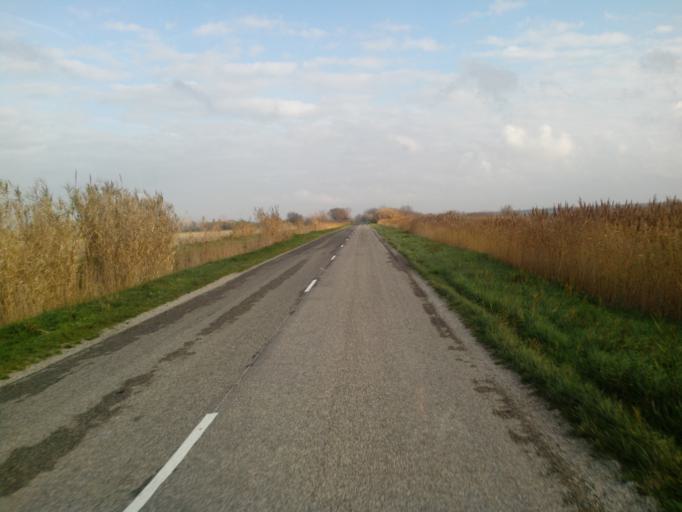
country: FR
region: Provence-Alpes-Cote d'Azur
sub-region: Departement des Bouches-du-Rhone
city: Arles
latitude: 43.5660
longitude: 4.5813
